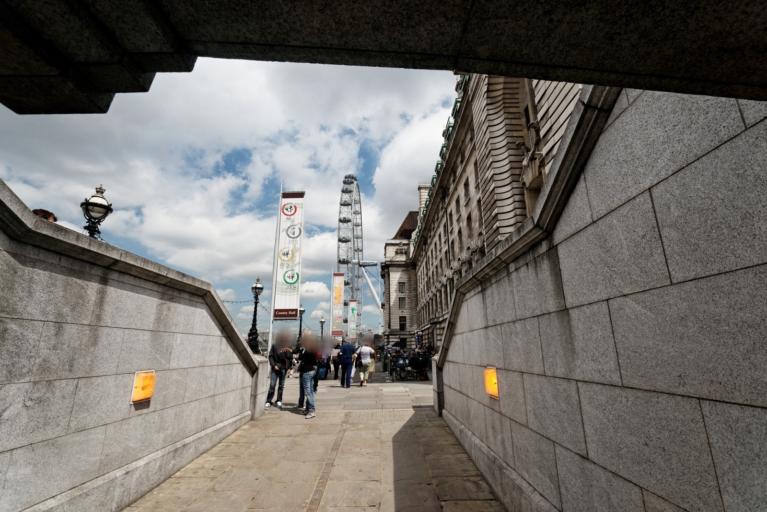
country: GB
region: England
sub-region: Greater London
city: City of Westminster
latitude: 51.5009
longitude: -0.1199
